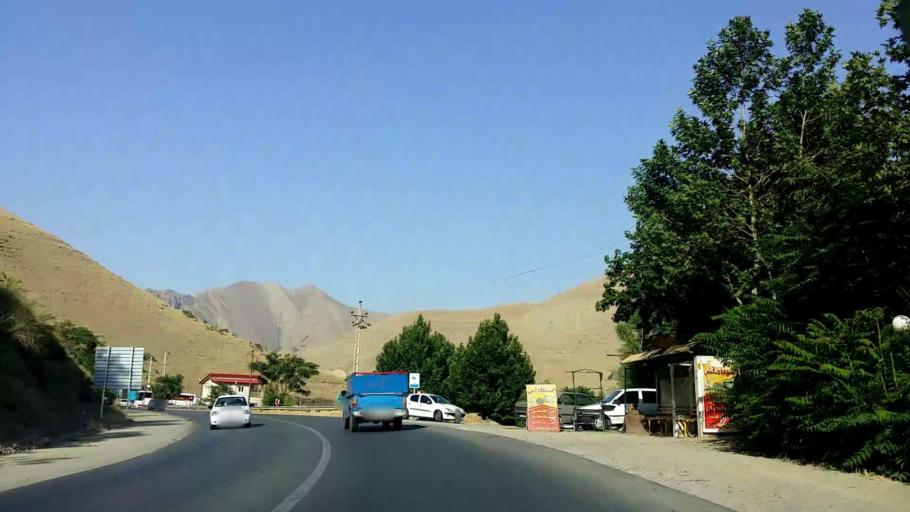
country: IR
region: Alborz
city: Karaj
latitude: 35.9347
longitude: 51.0673
